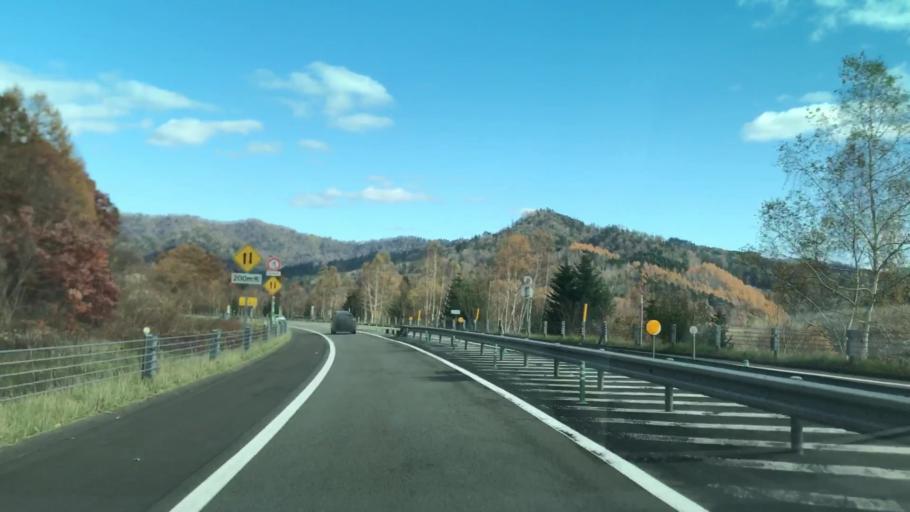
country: JP
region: Hokkaido
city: Chitose
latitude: 42.9054
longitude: 142.0043
